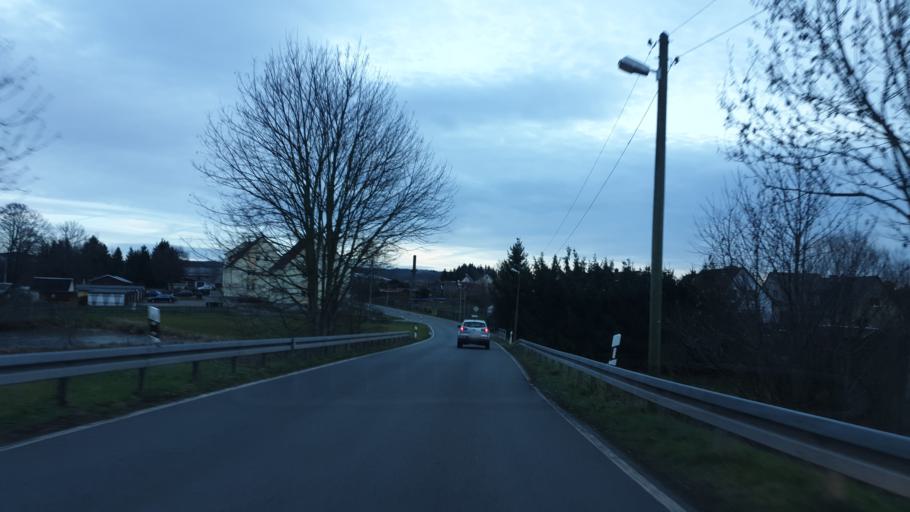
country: DE
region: Saxony
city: Hartenstein
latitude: 50.6756
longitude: 12.6651
